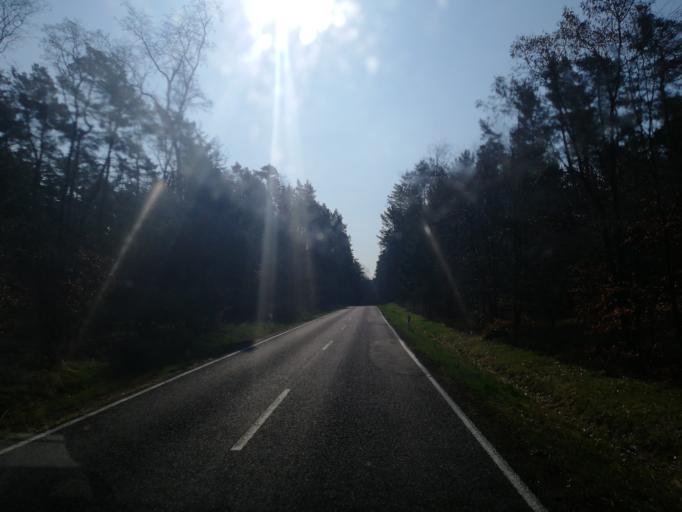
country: DE
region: Brandenburg
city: Sonnewalde
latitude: 51.7680
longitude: 13.6522
